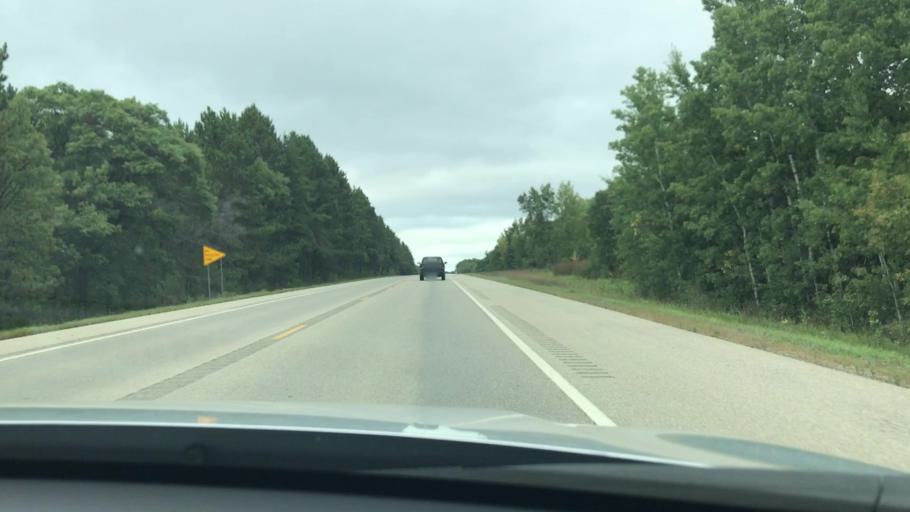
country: US
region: Minnesota
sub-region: Wadena County
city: Menahga
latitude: 46.8282
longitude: -95.0895
